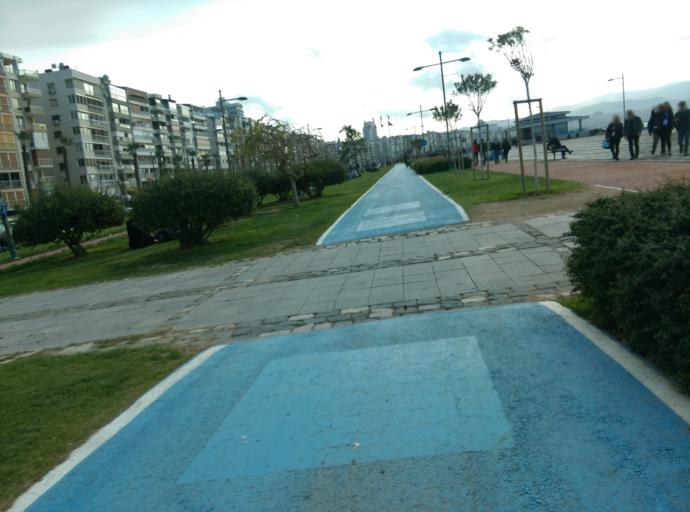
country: TR
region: Izmir
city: Izmir
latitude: 38.4401
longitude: 27.1418
